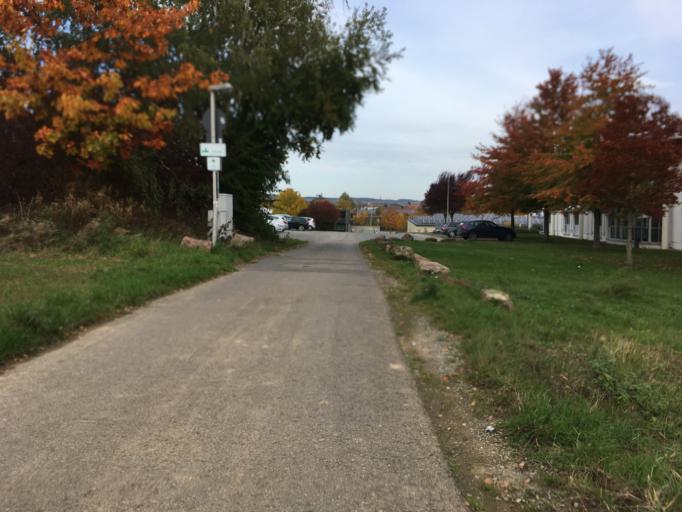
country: DE
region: Baden-Wuerttemberg
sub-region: Karlsruhe Region
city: Buchen
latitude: 49.5146
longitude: 9.3240
